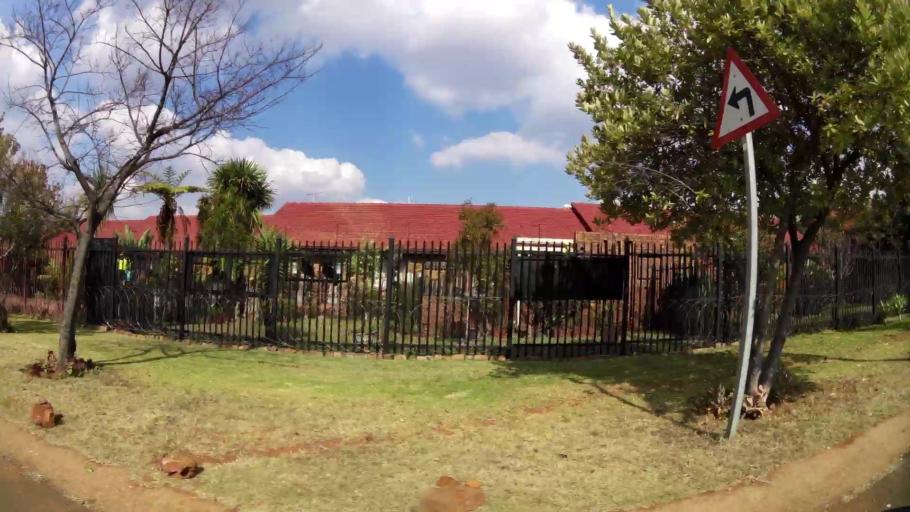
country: ZA
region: Gauteng
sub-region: City of Tshwane Metropolitan Municipality
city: Centurion
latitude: -25.8233
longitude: 28.2563
